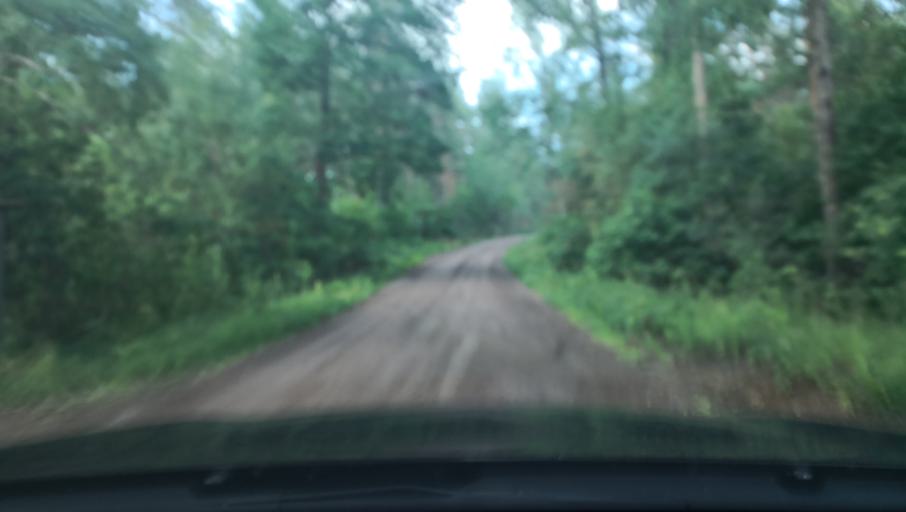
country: SE
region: Kalmar
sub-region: Hultsfreds Kommun
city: Malilla
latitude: 57.3902
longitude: 15.7514
